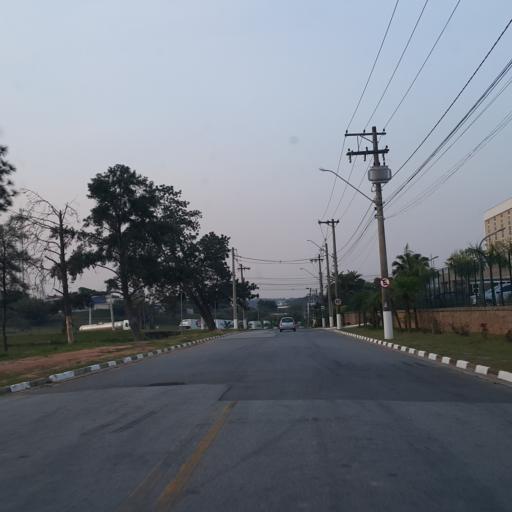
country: BR
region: Sao Paulo
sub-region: Vinhedo
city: Vinhedo
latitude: -23.0698
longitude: -47.0016
